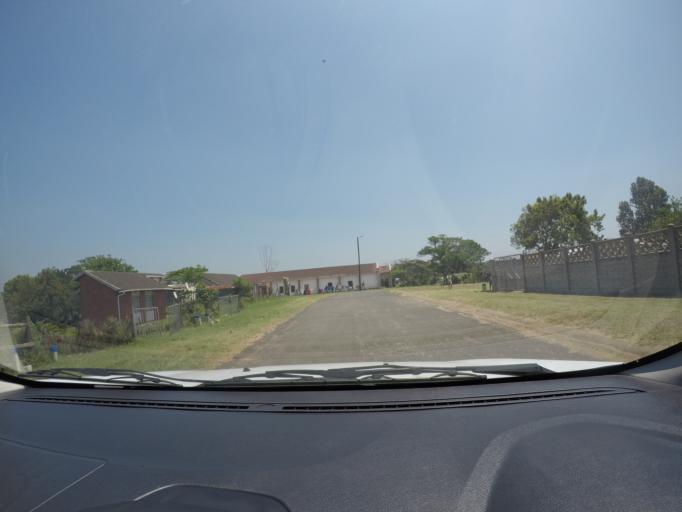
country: ZA
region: KwaZulu-Natal
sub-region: uThungulu District Municipality
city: eSikhawini
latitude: -28.8732
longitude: 31.9114
